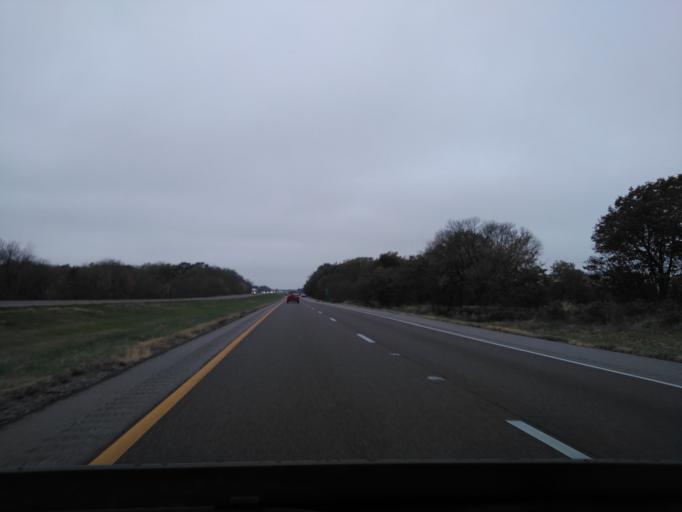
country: US
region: Illinois
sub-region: Madison County
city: Saint Jacob
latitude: 38.7659
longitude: -89.7644
